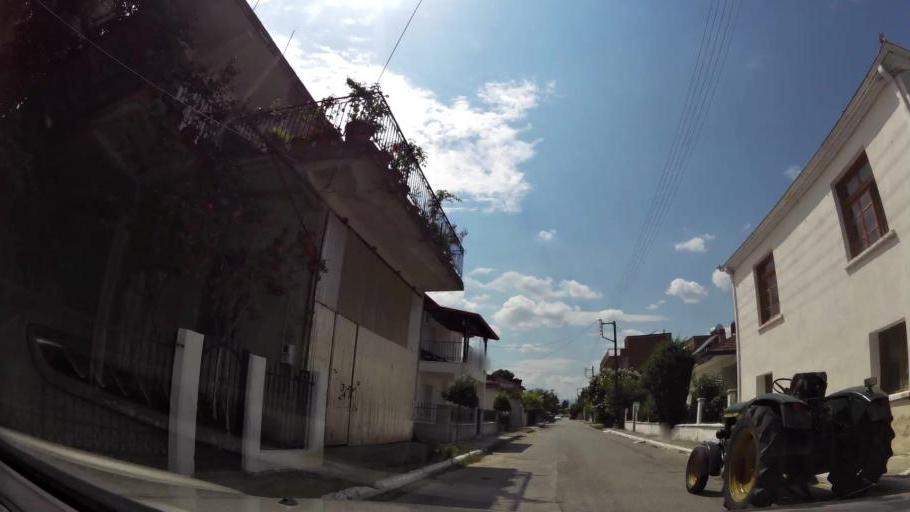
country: GR
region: Central Macedonia
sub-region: Nomos Pierias
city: Korinos
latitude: 40.3172
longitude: 22.5822
